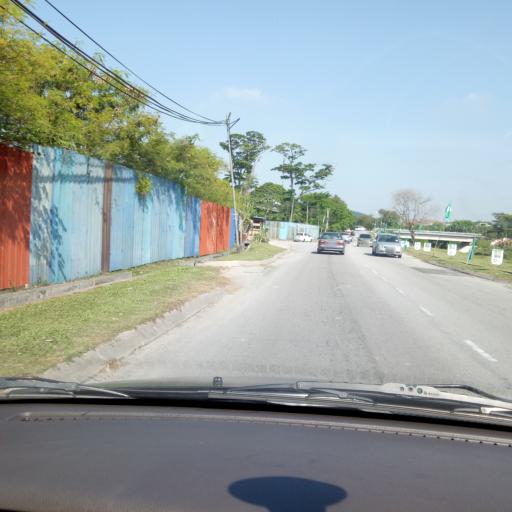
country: MY
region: Selangor
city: Kampong Baharu Balakong
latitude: 3.0154
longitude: 101.7653
